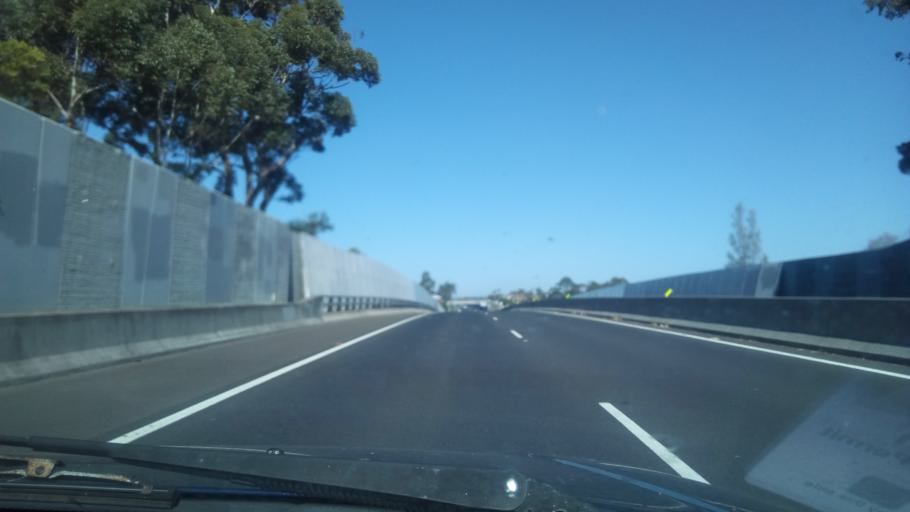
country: AU
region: New South Wales
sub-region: Wollongong
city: Bulli
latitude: -34.3429
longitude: 150.9107
